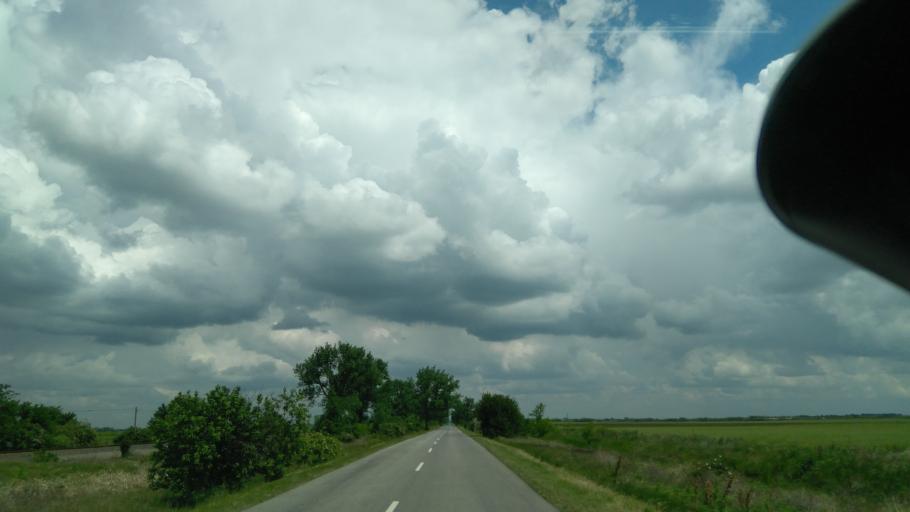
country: HU
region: Bekes
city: Devavanya
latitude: 47.0014
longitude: 20.9132
